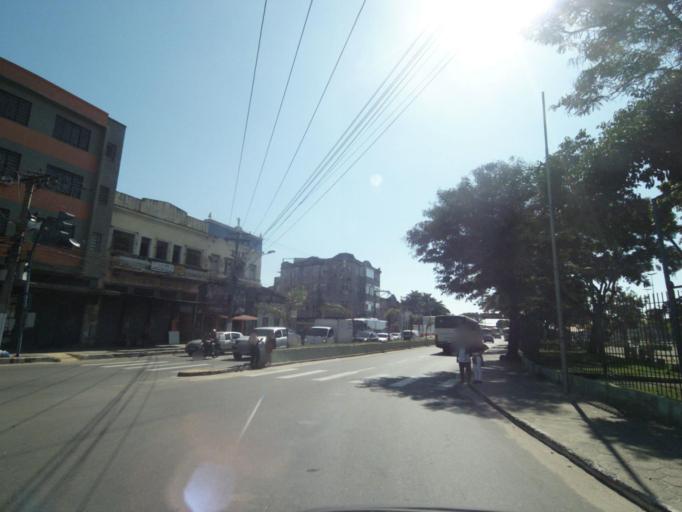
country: BR
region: Rio de Janeiro
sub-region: Niteroi
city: Niteroi
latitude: -22.8600
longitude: -43.1017
